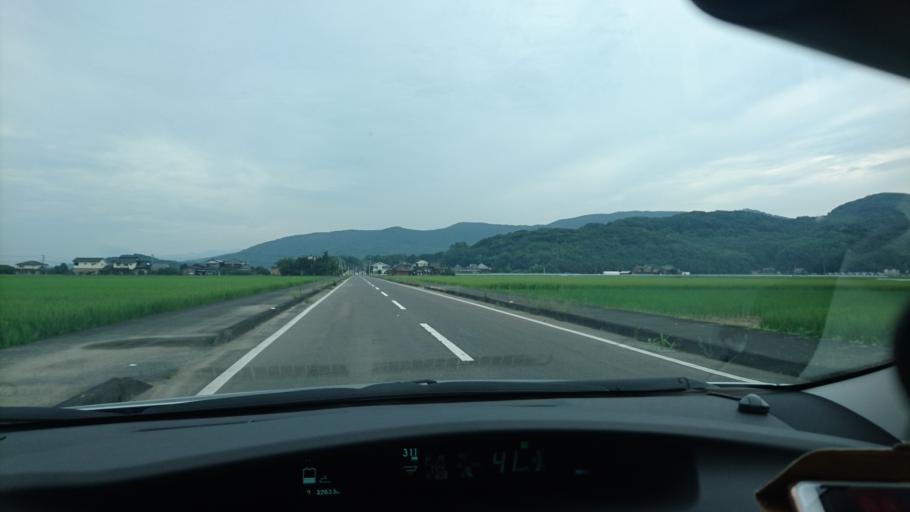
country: JP
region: Saga Prefecture
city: Takeocho-takeo
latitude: 33.1961
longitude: 130.1021
